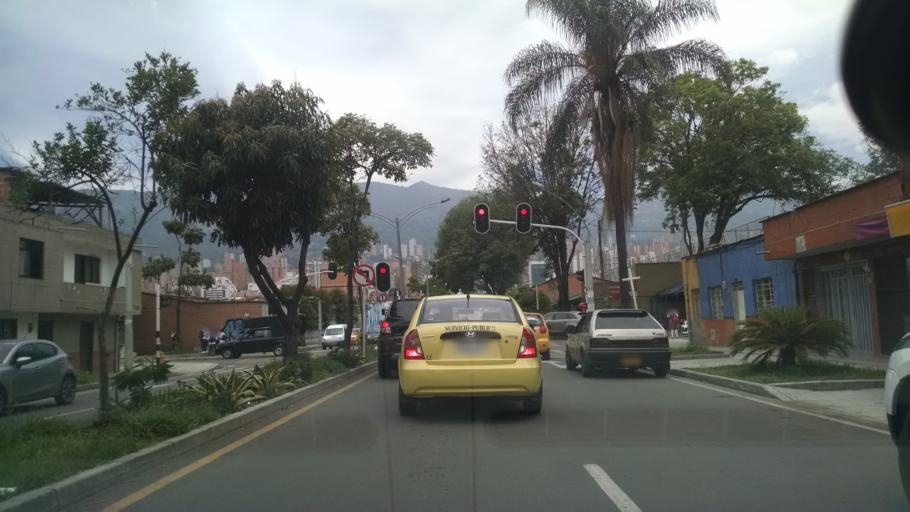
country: CO
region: Antioquia
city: Itagui
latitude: 6.2052
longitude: -75.5824
